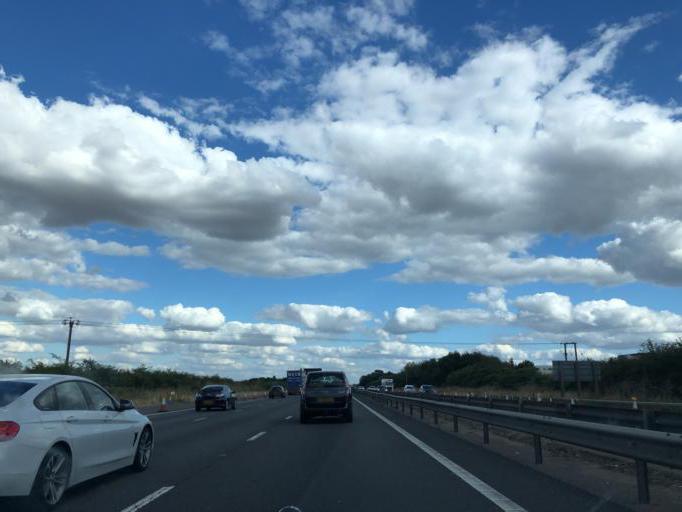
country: GB
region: England
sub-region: Milton Keynes
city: Newport Pagnell
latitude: 52.0721
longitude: -0.7283
